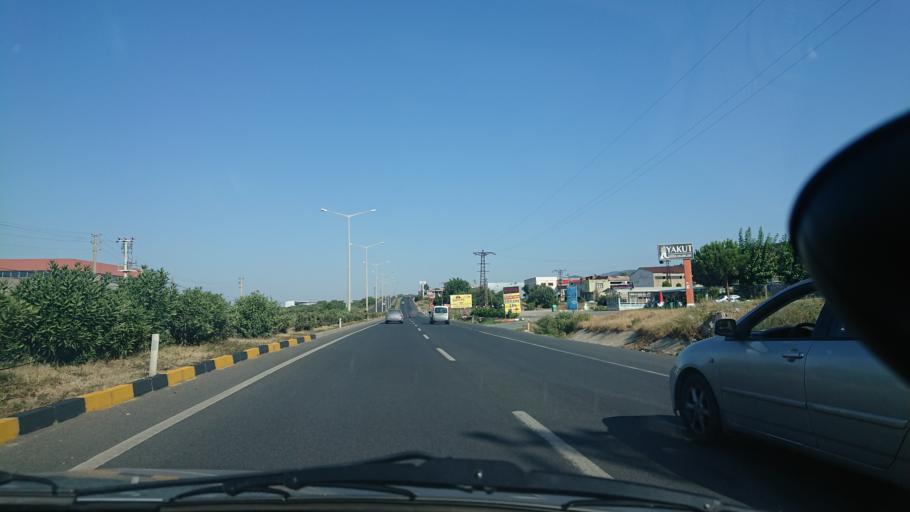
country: TR
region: Manisa
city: Turgutlu
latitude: 38.4953
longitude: 27.7700
